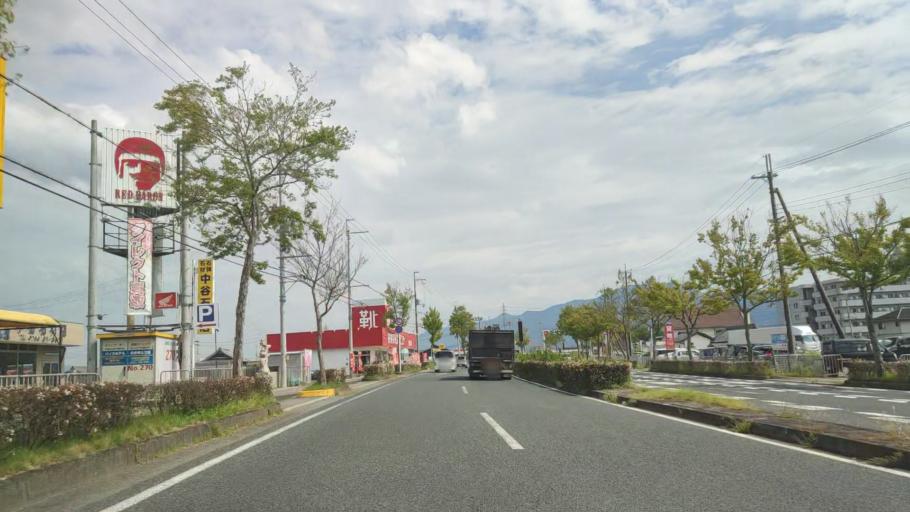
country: JP
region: Wakayama
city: Iwade
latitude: 34.2639
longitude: 135.3325
